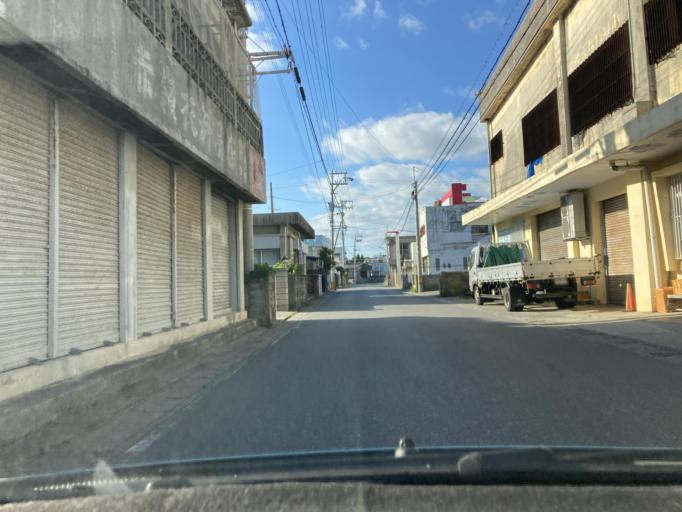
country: JP
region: Okinawa
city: Katsuren-haebaru
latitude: 26.3232
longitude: 127.9079
